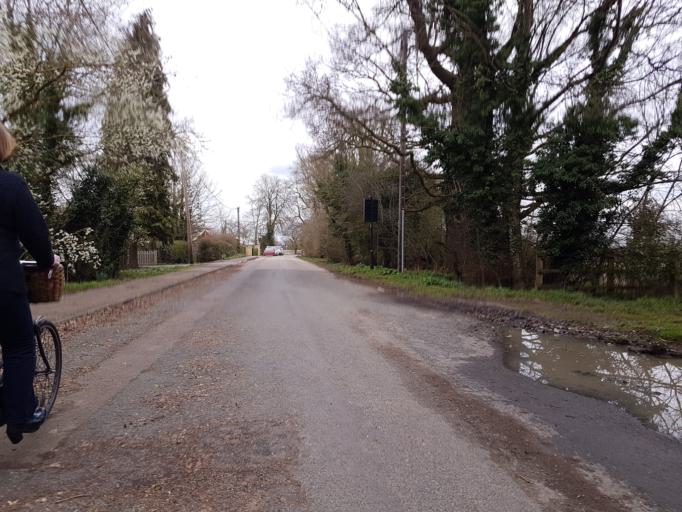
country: GB
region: England
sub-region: Cambridgeshire
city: Girton
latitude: 52.2279
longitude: 0.0437
